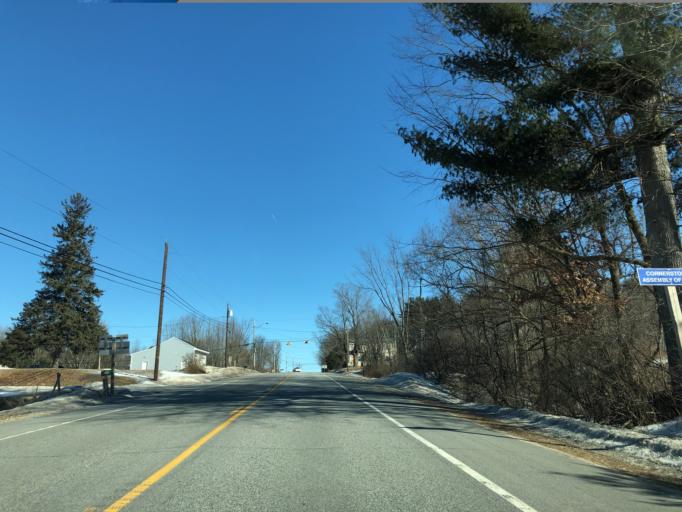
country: US
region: Maine
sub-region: Cumberland County
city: North Windham
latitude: 43.8236
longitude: -70.3898
